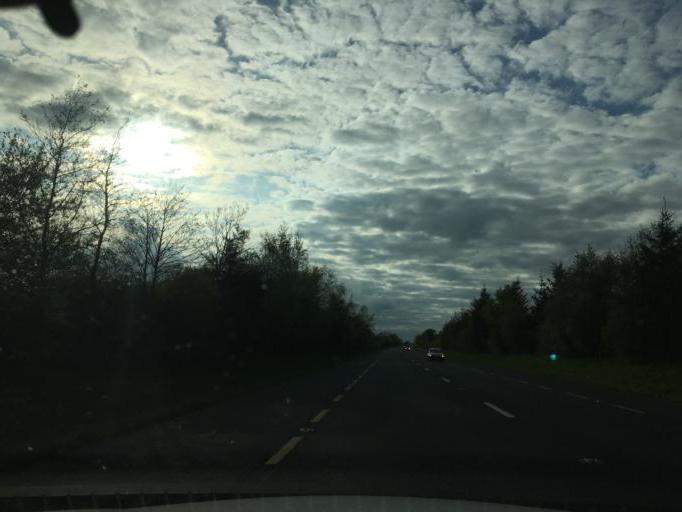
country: IE
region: Leinster
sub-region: Loch Garman
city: Enniscorthy
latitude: 52.3570
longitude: -6.6979
